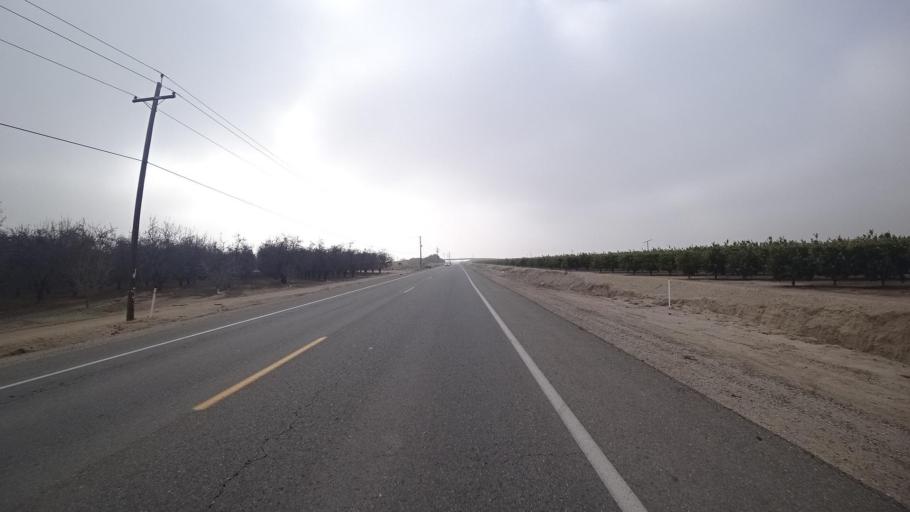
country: US
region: California
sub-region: Kern County
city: Pine Mountain Club
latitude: 35.0726
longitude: -119.1290
